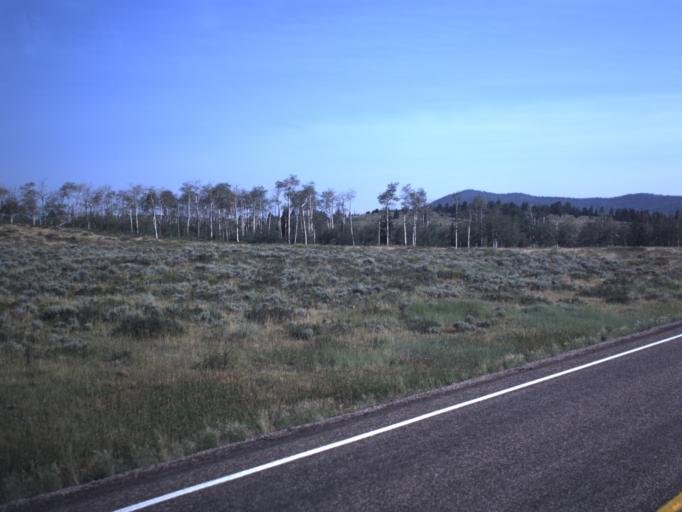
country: US
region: Utah
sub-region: Uintah County
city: Maeser
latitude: 40.6919
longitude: -109.4945
